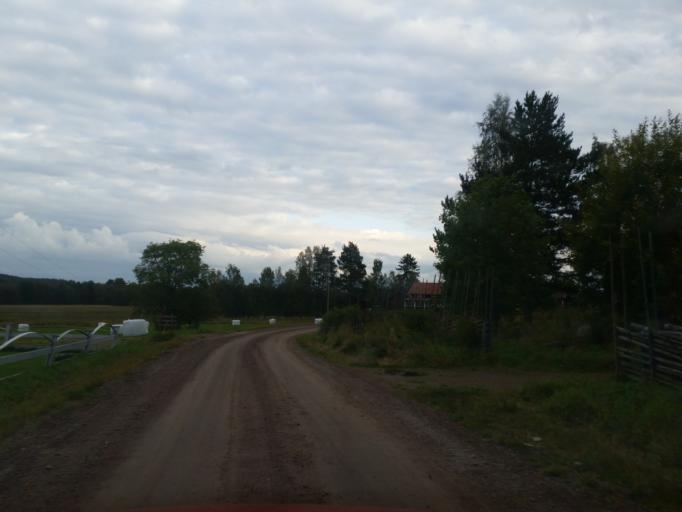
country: SE
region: Dalarna
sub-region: Leksand Municipality
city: Smedby
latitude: 60.6748
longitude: 15.1418
